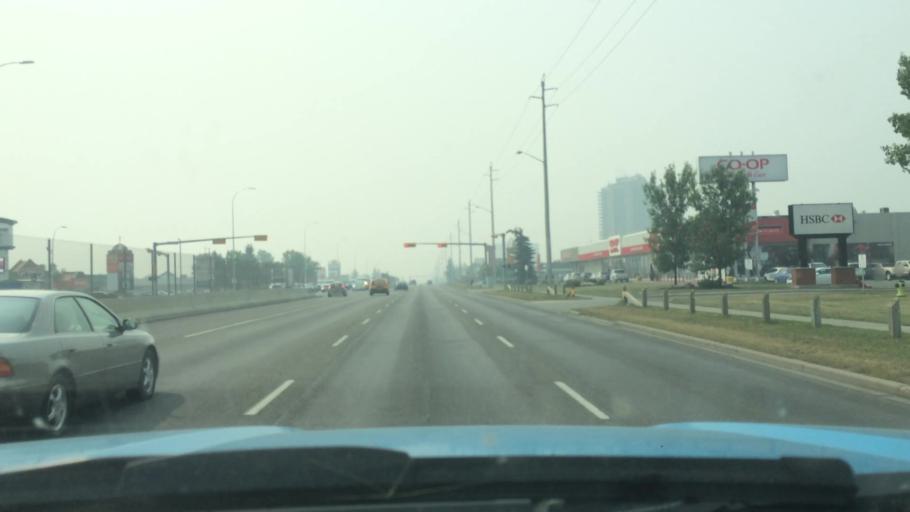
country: CA
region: Alberta
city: Calgary
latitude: 50.9732
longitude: -114.0717
